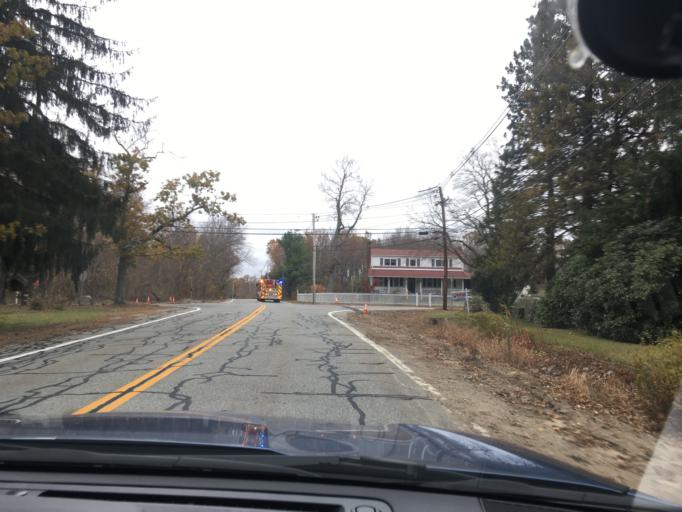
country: US
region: Rhode Island
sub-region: Providence County
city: North Scituate
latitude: 41.8123
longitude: -71.6608
